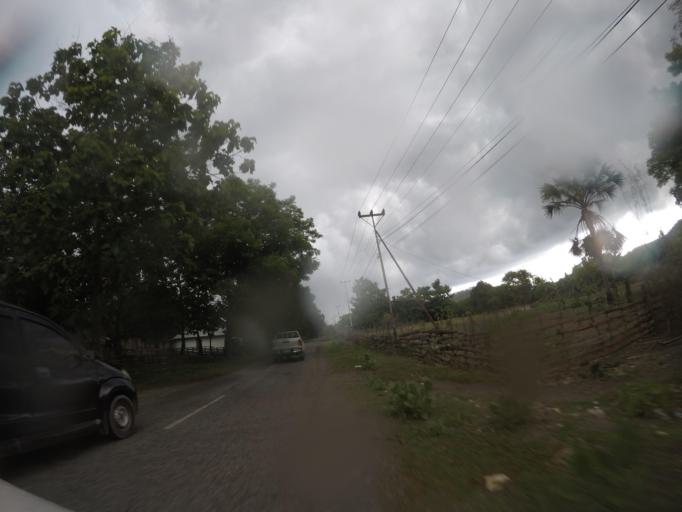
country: ID
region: East Nusa Tenggara
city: Atambua
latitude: -8.9660
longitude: 125.0002
